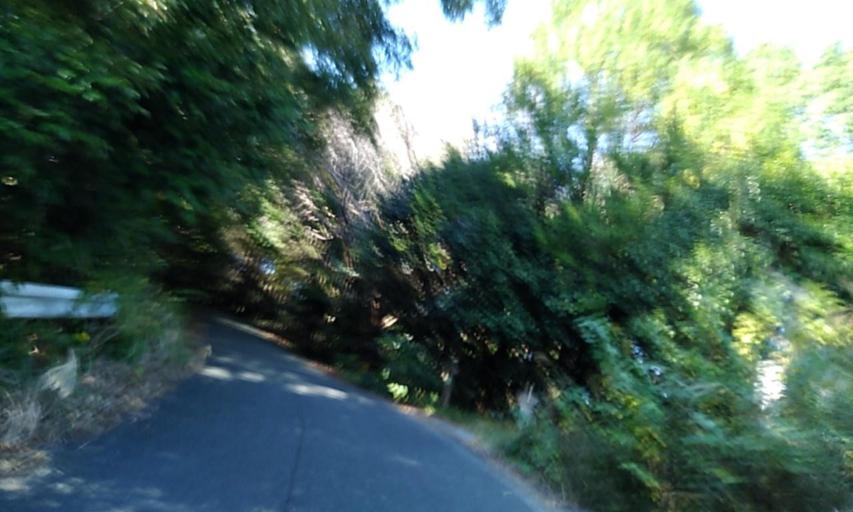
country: JP
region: Shizuoka
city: Hamakita
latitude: 34.8132
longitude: 137.6487
